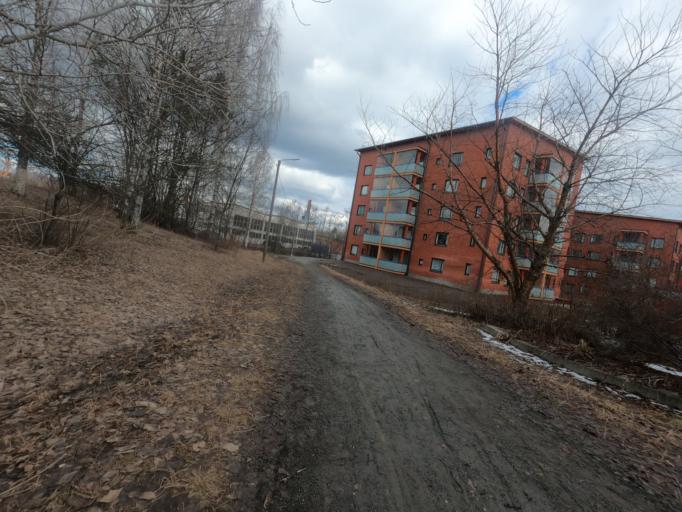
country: FI
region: North Karelia
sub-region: Joensuu
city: Joensuu
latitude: 62.5984
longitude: 29.7825
